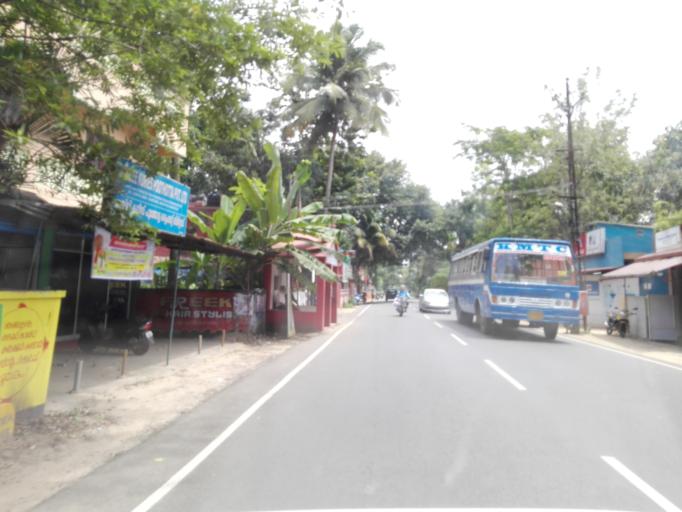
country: IN
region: Kerala
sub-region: Alappuzha
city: Arukutti
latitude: 9.8579
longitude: 76.3833
